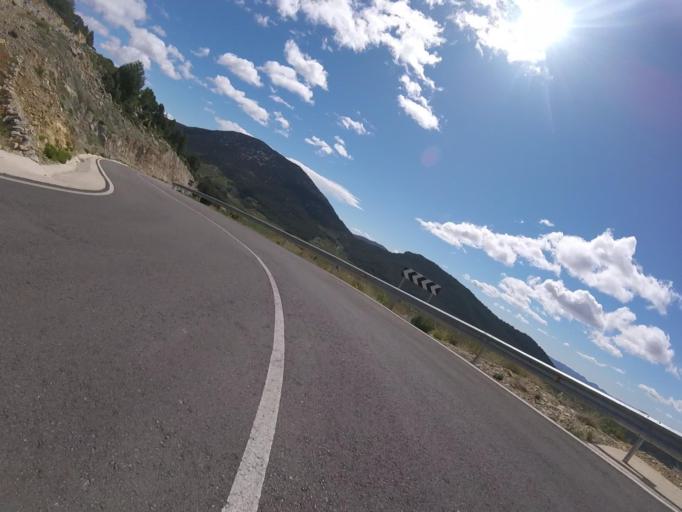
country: ES
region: Valencia
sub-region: Provincia de Castello
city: Culla
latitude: 40.2929
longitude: -0.1212
